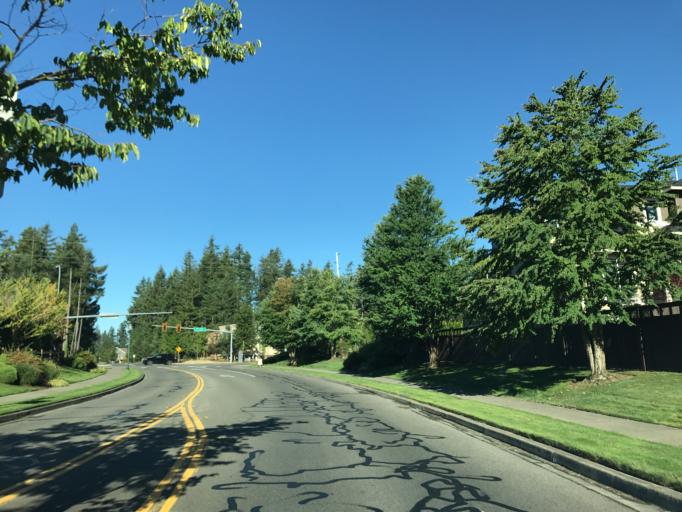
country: US
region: Washington
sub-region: King County
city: Ravensdale
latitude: 47.3542
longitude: -122.0181
